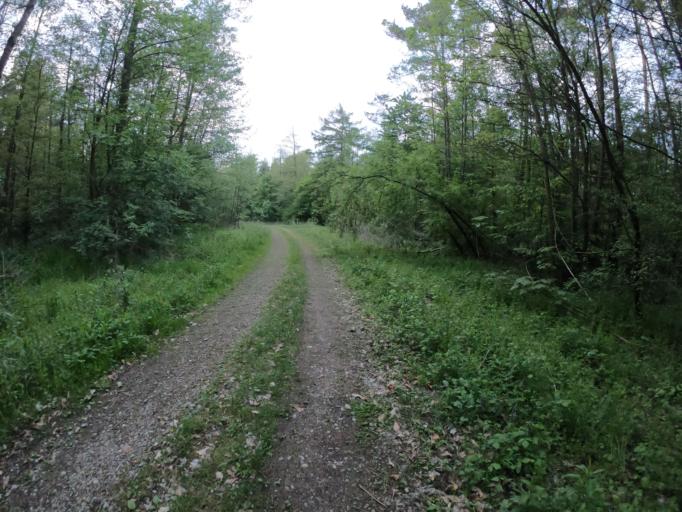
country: DE
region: Bavaria
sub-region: Upper Franconia
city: Memmelsdorf
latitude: 49.9187
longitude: 10.9371
